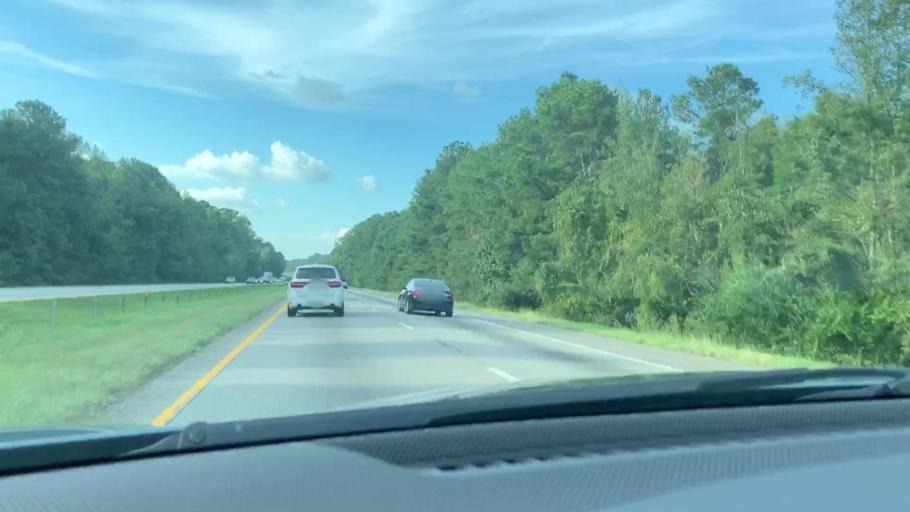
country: US
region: South Carolina
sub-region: Orangeburg County
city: Brookdale
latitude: 33.4899
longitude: -80.7623
